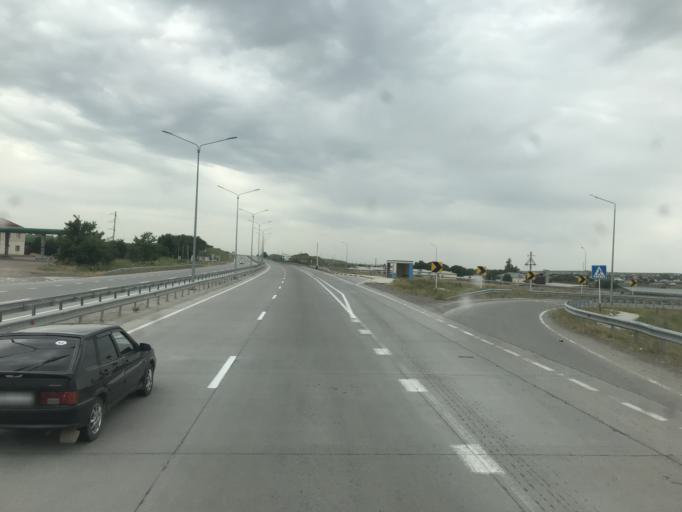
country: KZ
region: Ongtustik Qazaqstan
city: Qazyqurt
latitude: 41.7578
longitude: 69.4011
